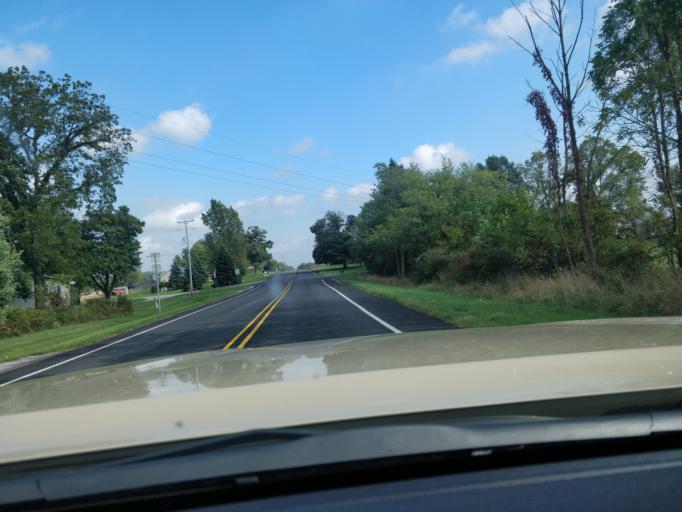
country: US
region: Michigan
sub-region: Ionia County
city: Saranac
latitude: 42.8861
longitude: -85.1749
